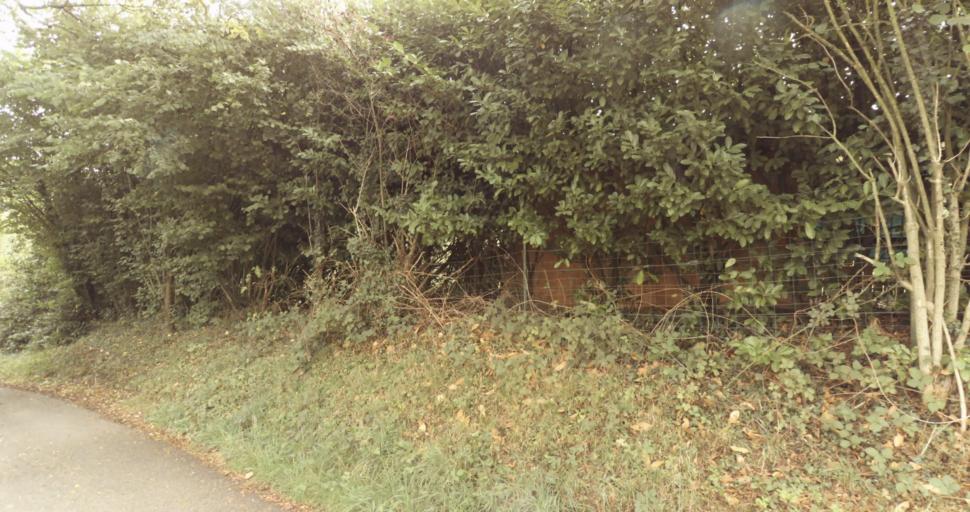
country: FR
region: Lower Normandy
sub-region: Departement de l'Orne
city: Gace
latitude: 48.8051
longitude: 0.3254
